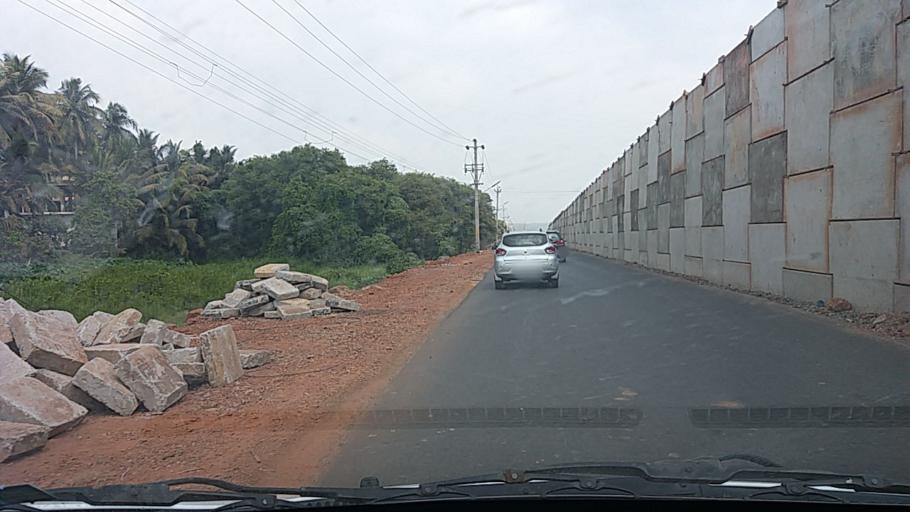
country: IN
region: Goa
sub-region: North Goa
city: Bambolim
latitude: 15.4795
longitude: 73.8481
